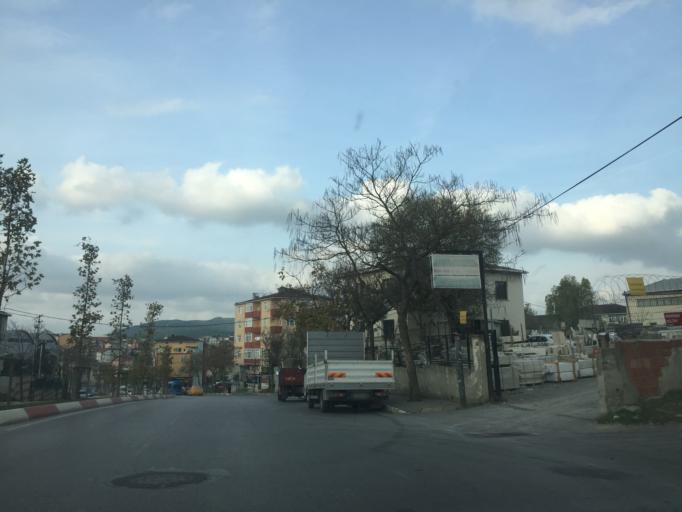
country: TR
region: Istanbul
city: Sultanbeyli
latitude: 40.9438
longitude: 29.3004
